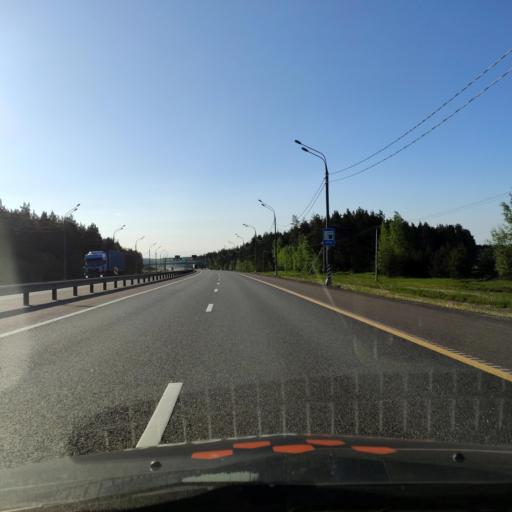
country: RU
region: Lipetsk
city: Zadonsk
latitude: 52.3793
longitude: 38.8813
